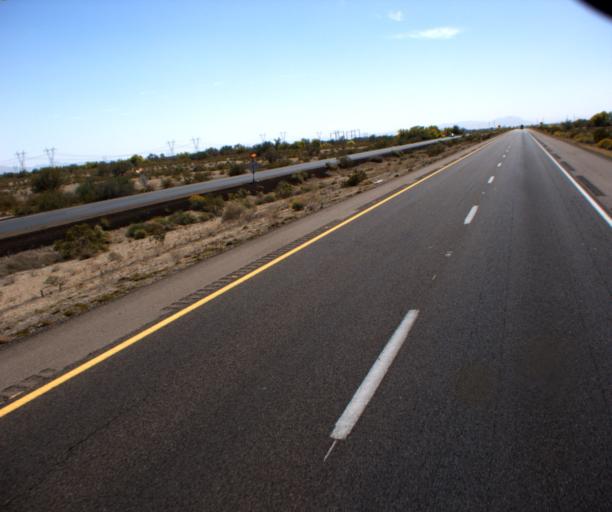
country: US
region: Arizona
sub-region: Maricopa County
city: Gila Bend
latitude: 32.9934
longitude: -112.6627
